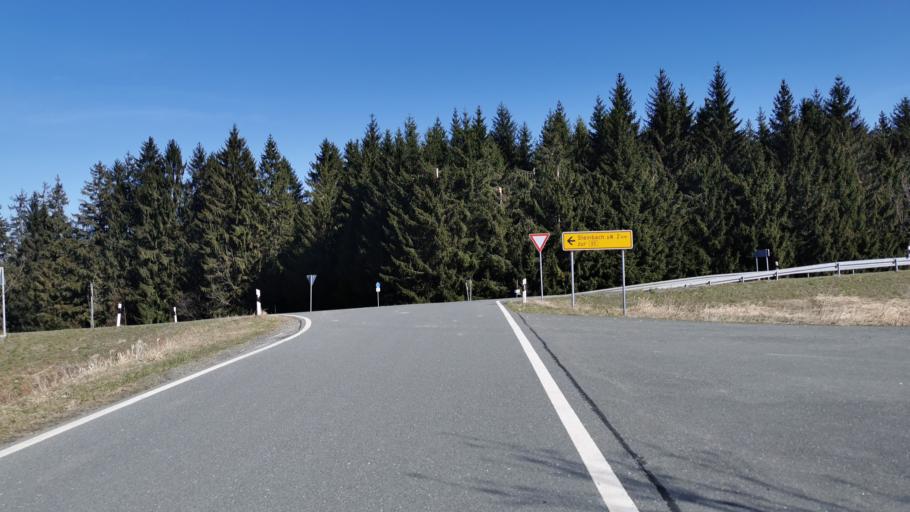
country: DE
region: Bavaria
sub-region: Upper Franconia
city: Reichenbach
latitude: 50.4475
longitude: 11.4046
